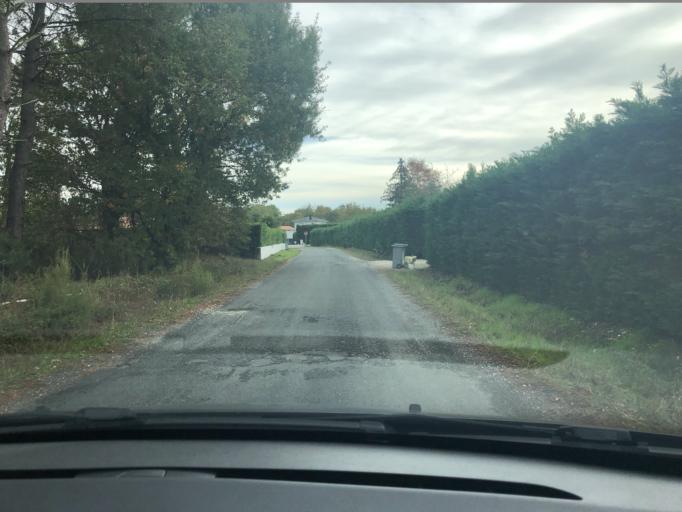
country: FR
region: Aquitaine
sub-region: Departement de la Gironde
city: Le Pian-Medoc
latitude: 44.9486
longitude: -0.6495
